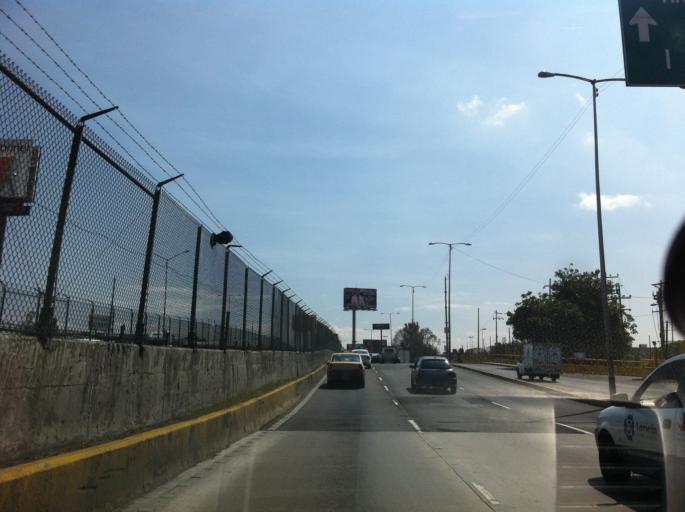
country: MX
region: Mexico City
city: Venustiano Carranza
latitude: 19.4508
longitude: -99.1039
